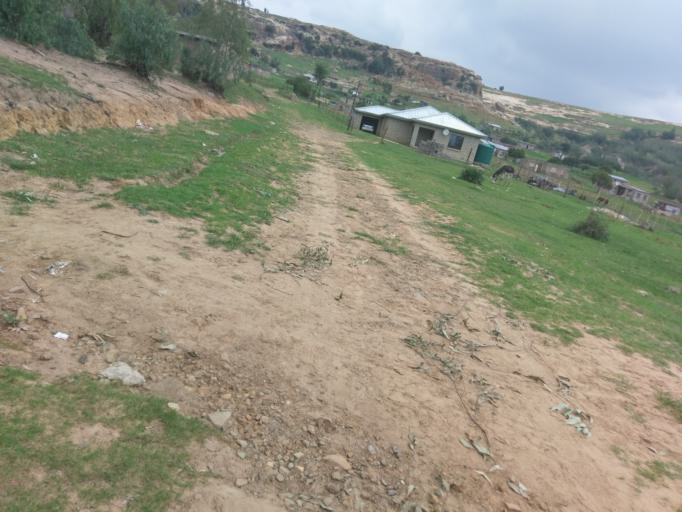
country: LS
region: Leribe
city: Leribe
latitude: -29.0312
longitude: 28.0220
